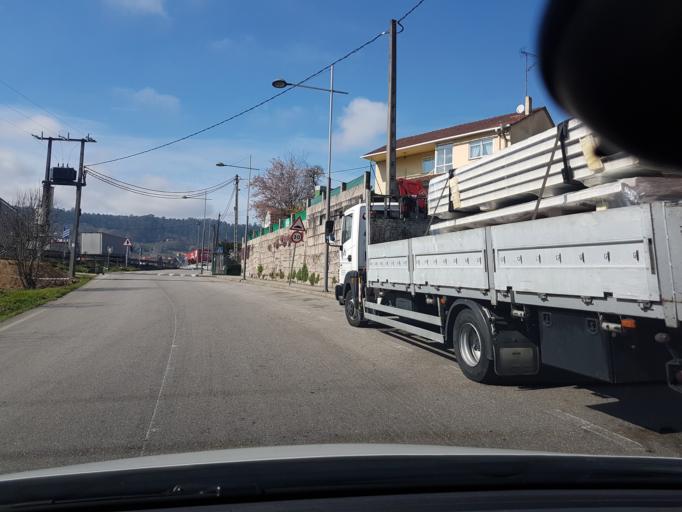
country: ES
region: Galicia
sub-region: Provincia de Pontevedra
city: Porrino
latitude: 42.1949
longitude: -8.6456
